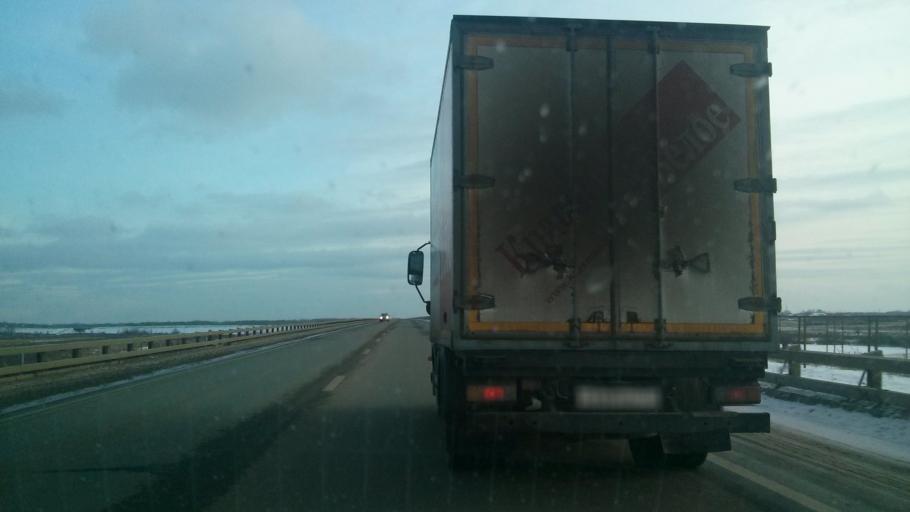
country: RU
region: Vladimir
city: Murom
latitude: 55.5913
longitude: 42.1167
